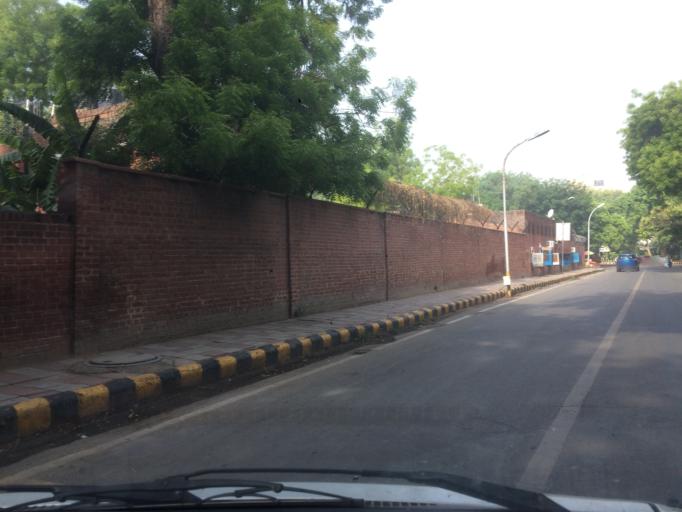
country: IN
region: NCT
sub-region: New Delhi
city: New Delhi
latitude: 28.6279
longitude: 77.2354
